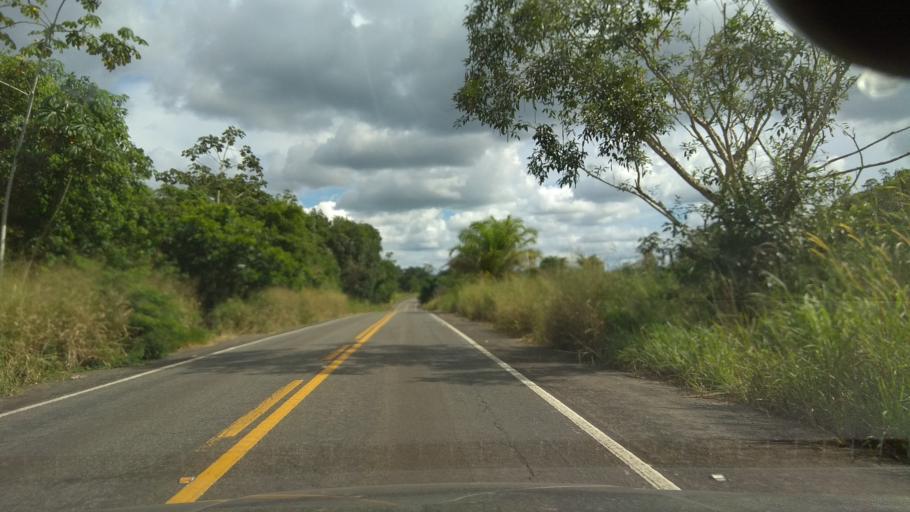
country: BR
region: Bahia
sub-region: Ubaitaba
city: Ubaitaba
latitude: -14.2495
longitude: -39.3653
